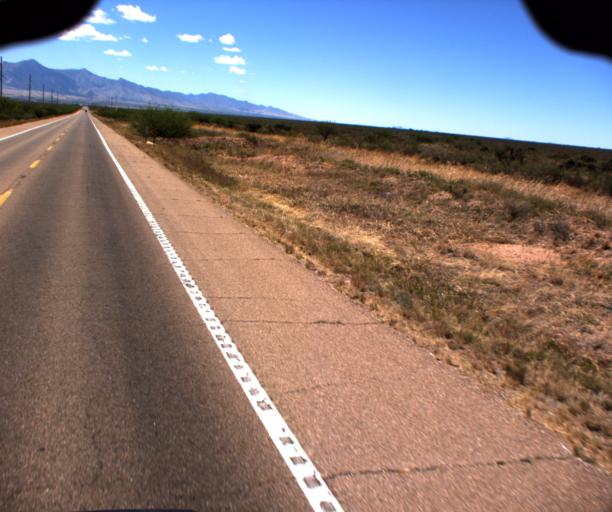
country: US
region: Arizona
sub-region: Cochise County
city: Naco
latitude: 31.3745
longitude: -109.9962
